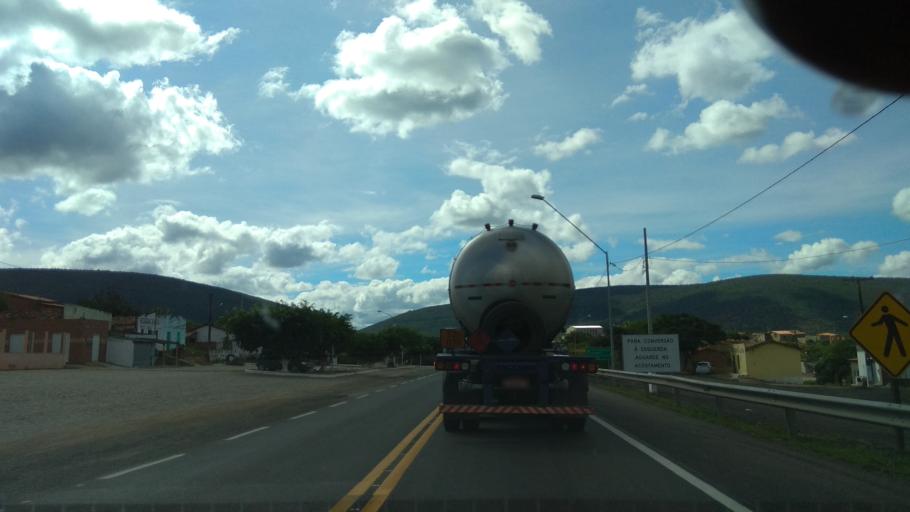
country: BR
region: Bahia
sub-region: Santa Ines
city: Santa Ines
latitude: -13.2744
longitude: -40.0146
